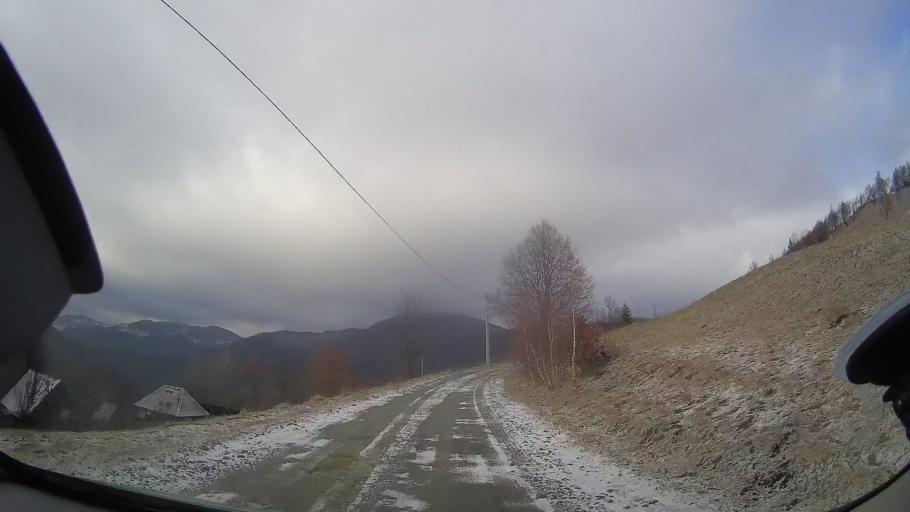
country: RO
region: Cluj
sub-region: Comuna Valea Ierii
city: Valea Ierii
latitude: 46.6488
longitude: 23.3570
